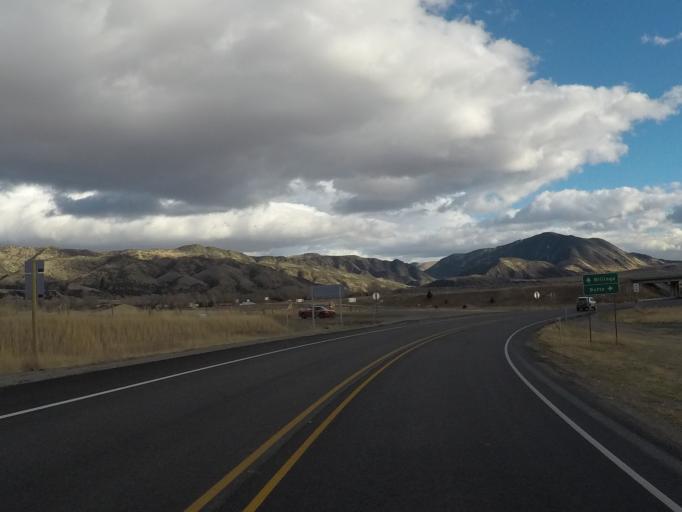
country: US
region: Montana
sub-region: Jefferson County
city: Whitehall
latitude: 45.8713
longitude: -111.9554
